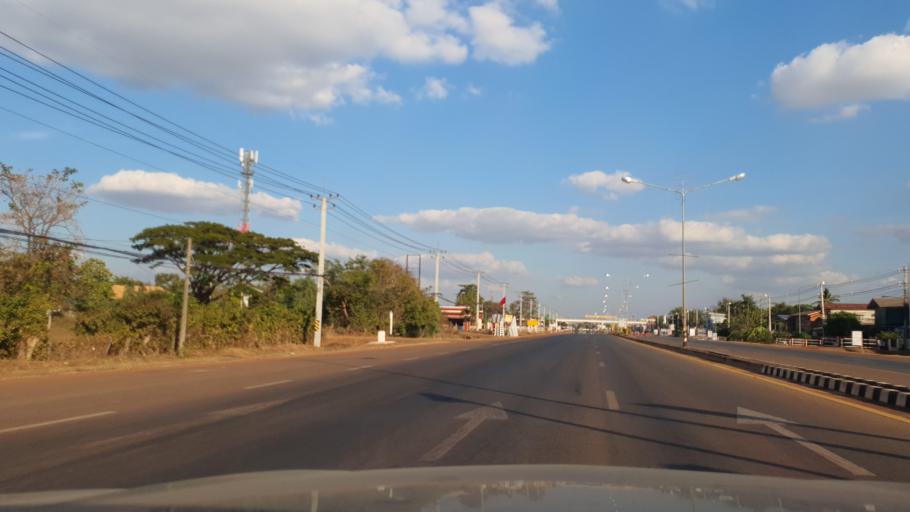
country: TH
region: Sakon Nakhon
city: Sakon Nakhon
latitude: 17.2563
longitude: 104.1802
